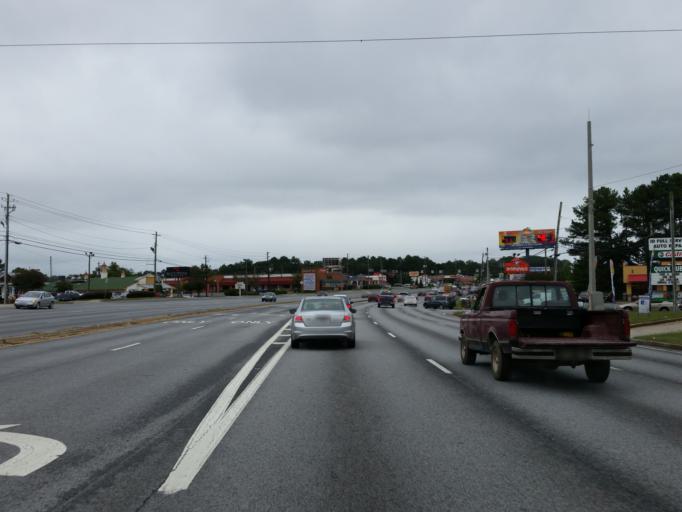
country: US
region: Georgia
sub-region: Clayton County
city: Morrow
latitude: 33.5765
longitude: -84.3726
